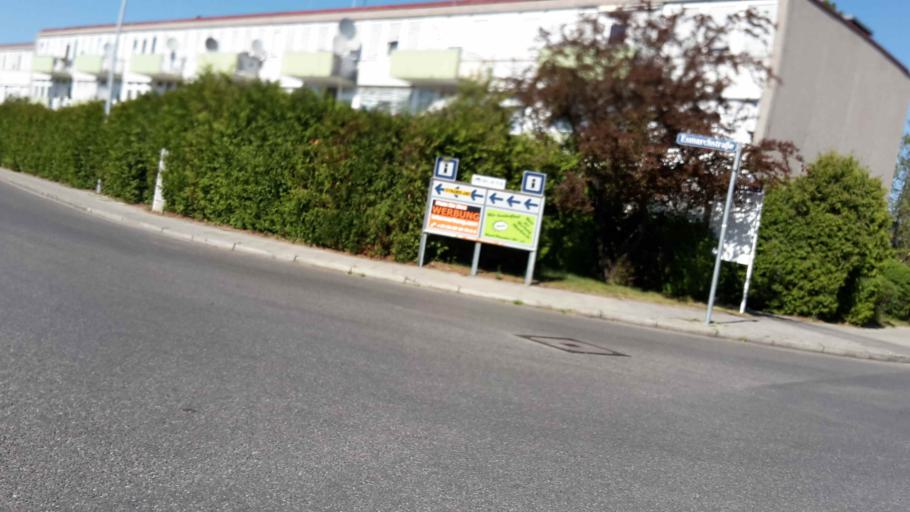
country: DE
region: Bavaria
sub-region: Upper Bavaria
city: Karlsfeld
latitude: 48.1855
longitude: 11.4664
